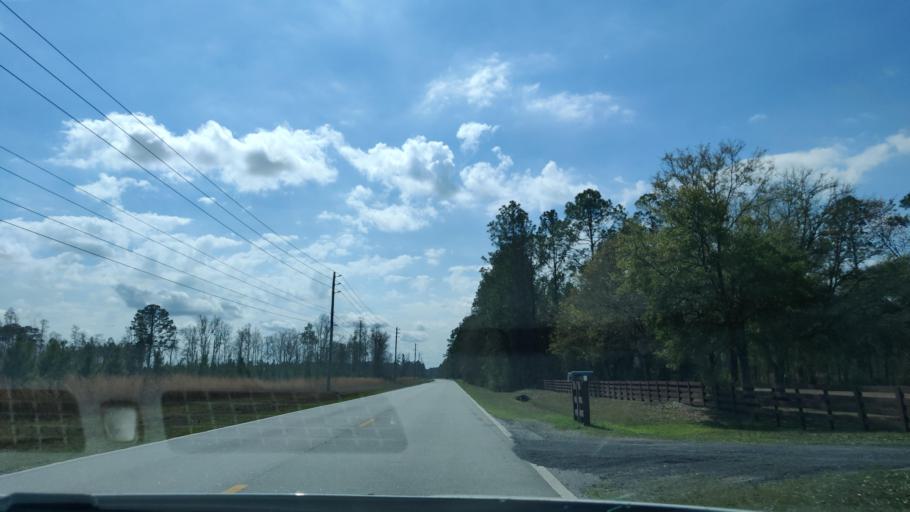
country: US
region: Florida
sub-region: Duval County
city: Baldwin
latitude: 30.2330
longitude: -81.9411
